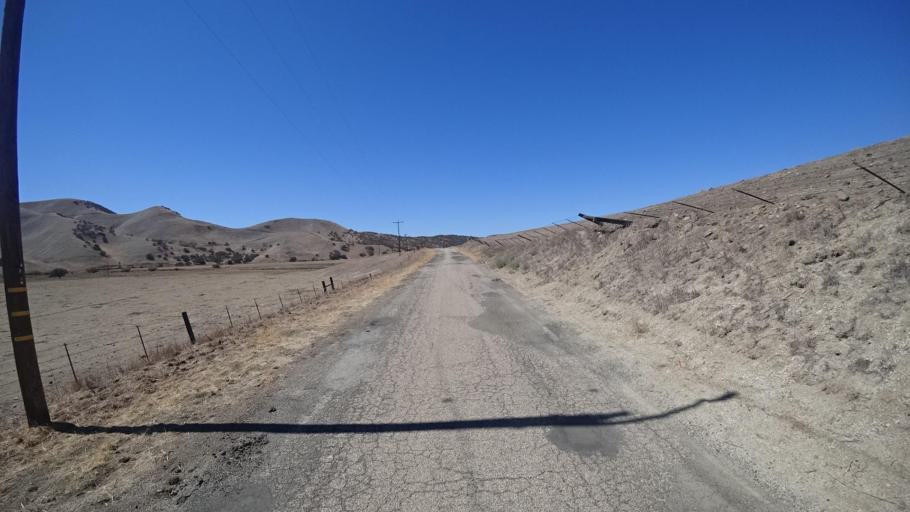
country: US
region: California
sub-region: Monterey County
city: King City
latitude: 36.2798
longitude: -120.9512
